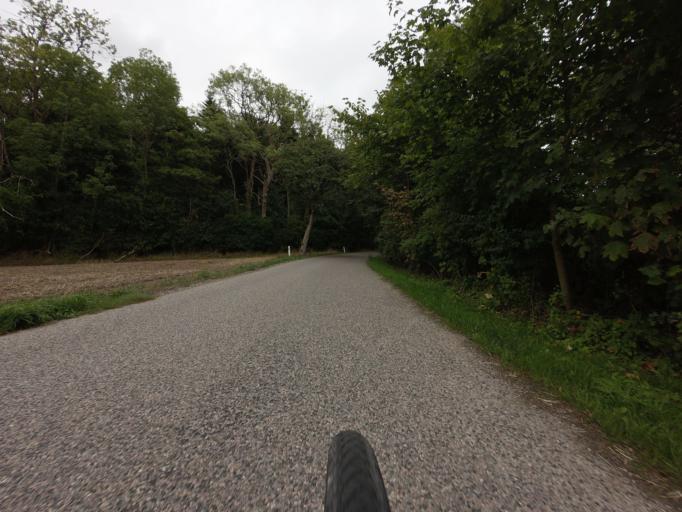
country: DK
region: Zealand
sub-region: Stevns Kommune
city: Store Heddinge
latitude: 55.3159
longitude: 12.3406
